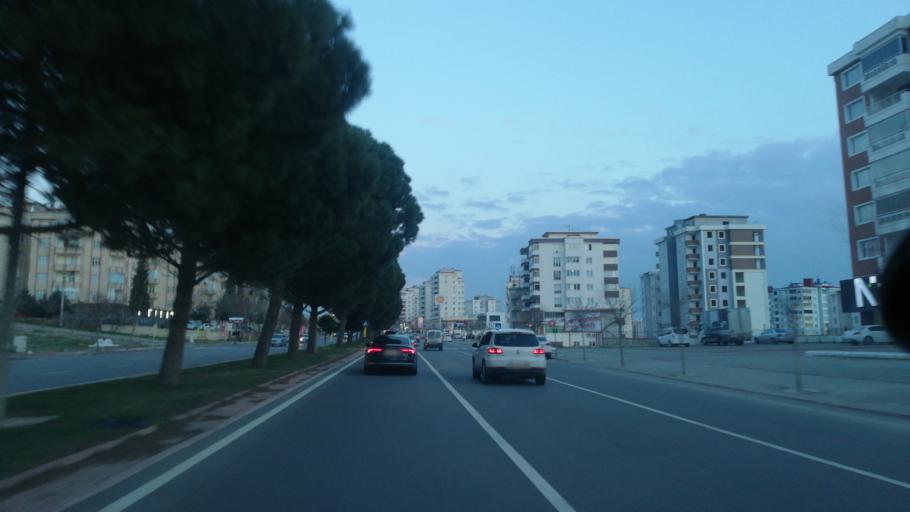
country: TR
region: Kahramanmaras
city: Kahramanmaras
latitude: 37.5946
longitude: 36.8545
